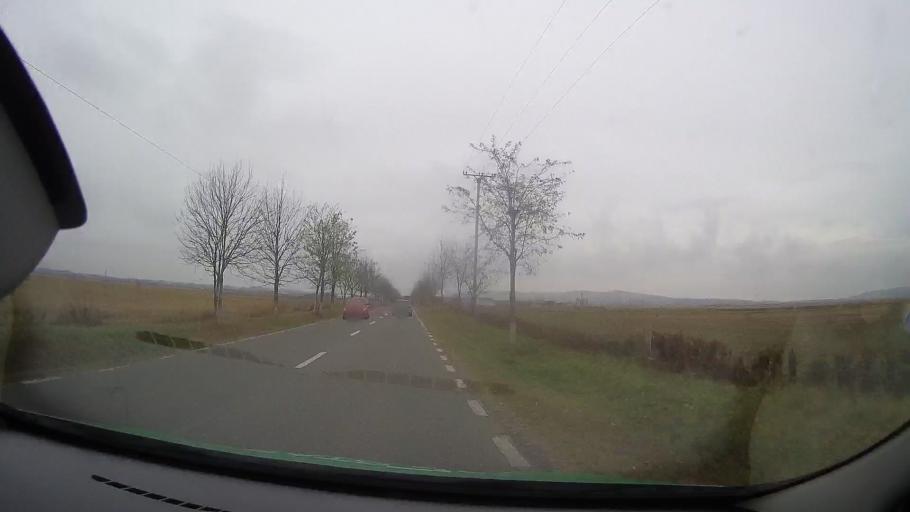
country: RO
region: Prahova
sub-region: Oras Baicoi
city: Liliesti
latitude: 45.0107
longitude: 25.8844
